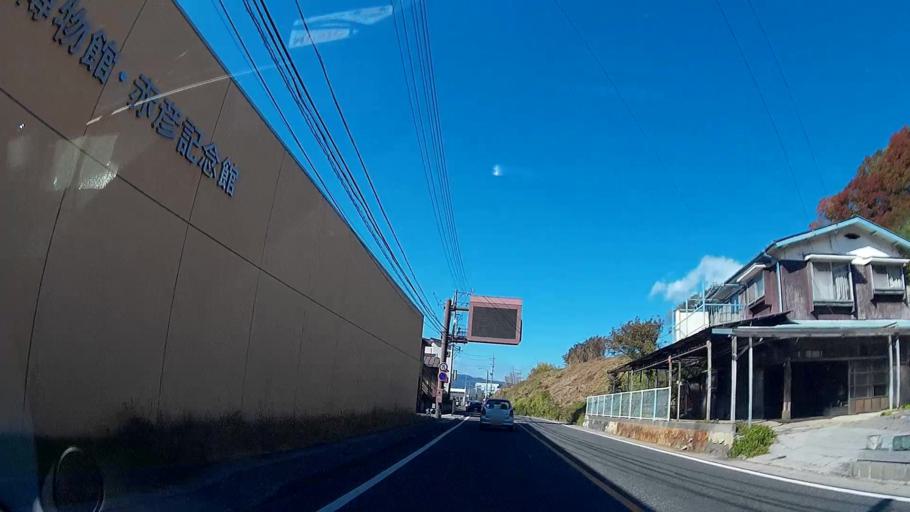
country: JP
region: Nagano
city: Suwa
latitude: 36.0674
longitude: 138.1011
